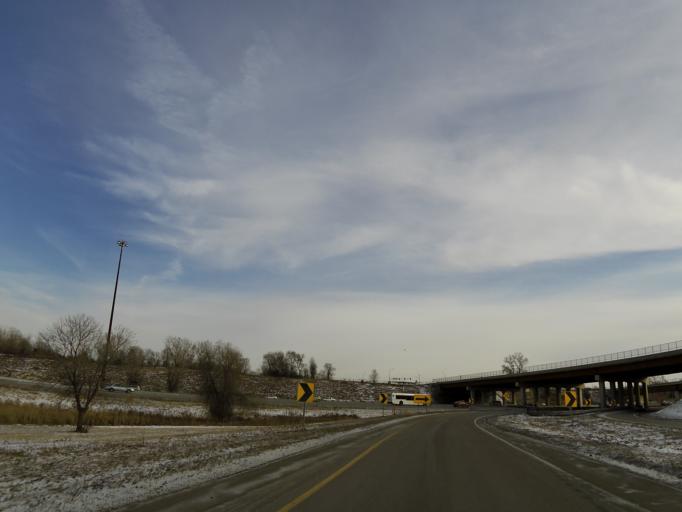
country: US
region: Minnesota
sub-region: Dakota County
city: Mendota Heights
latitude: 44.8603
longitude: -93.1471
